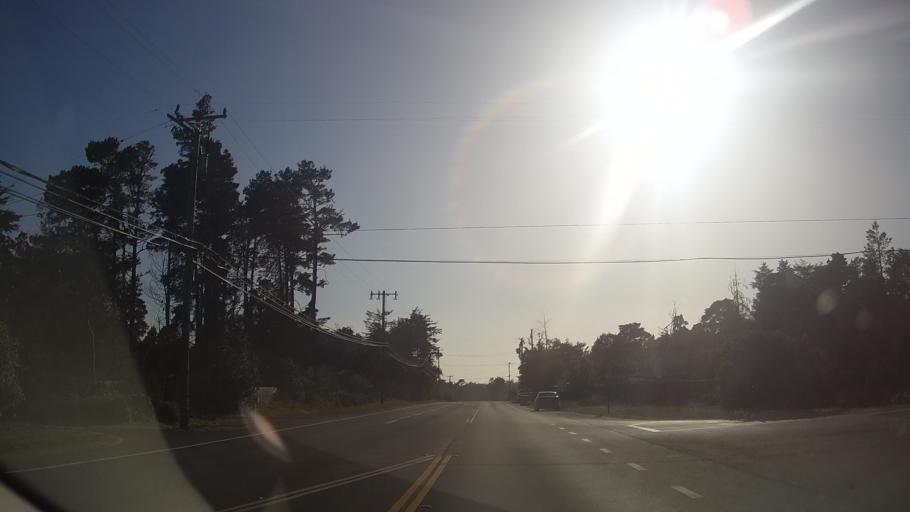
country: US
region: California
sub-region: Mendocino County
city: Fort Bragg
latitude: 39.4155
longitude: -123.7779
